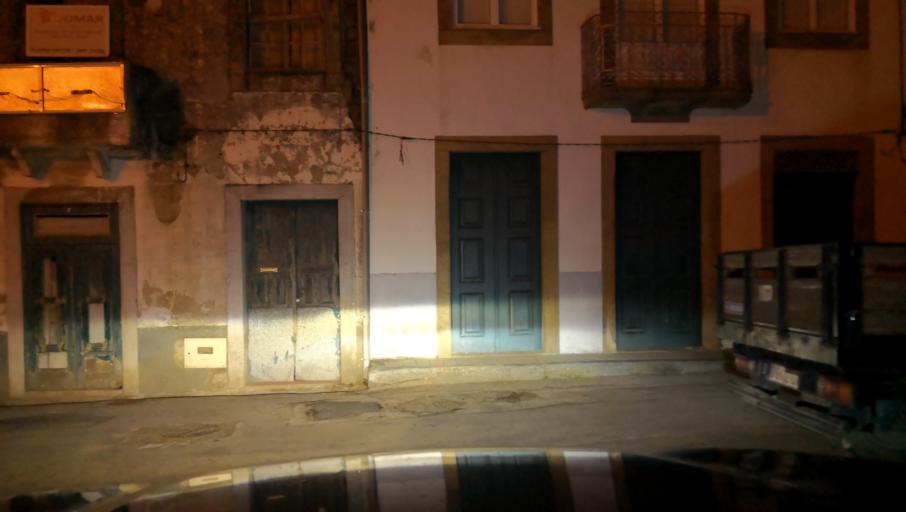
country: PT
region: Vila Real
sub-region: Peso da Regua
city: Peso da Regua
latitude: 41.1651
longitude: -7.7286
